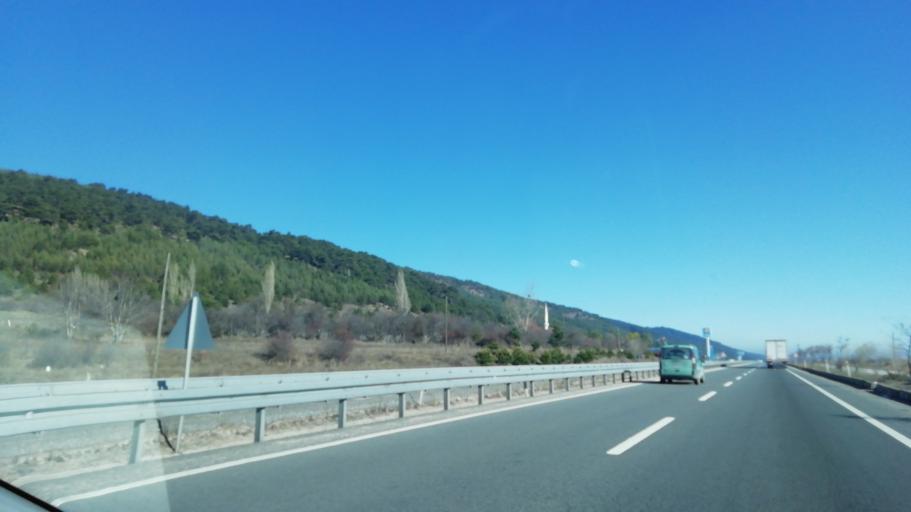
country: TR
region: Bolu
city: Gerede
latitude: 40.8166
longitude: 32.2904
